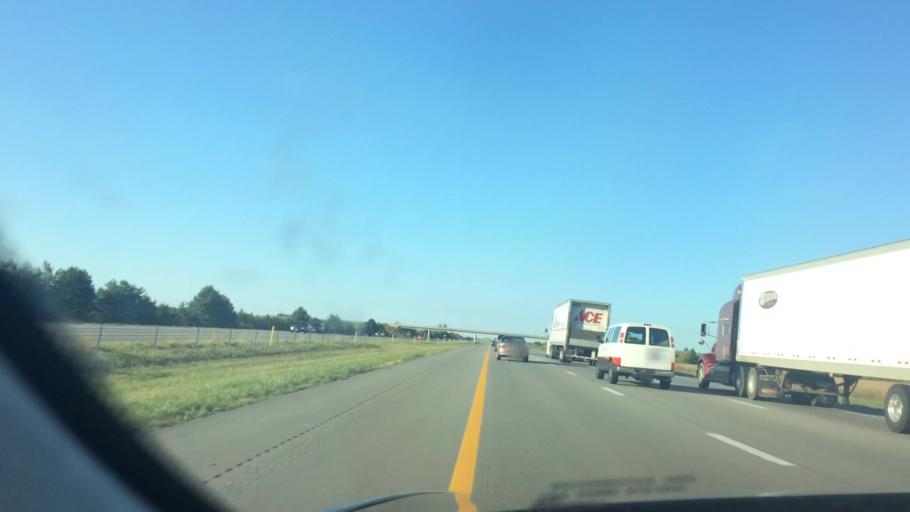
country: US
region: Ohio
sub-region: Wood County
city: Bowling Green
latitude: 41.4064
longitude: -83.6158
